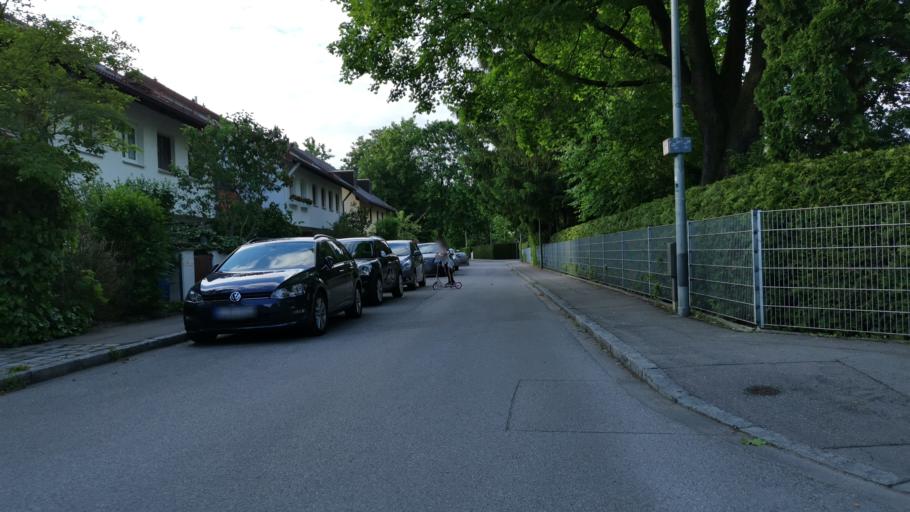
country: DE
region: Bavaria
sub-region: Upper Bavaria
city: Neuried
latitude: 48.0780
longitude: 11.4924
